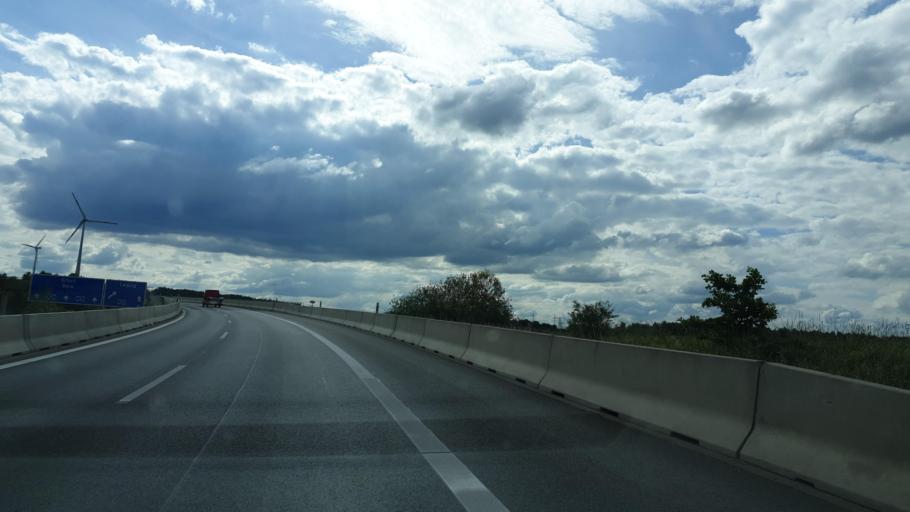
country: DE
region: Saxony
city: Wittgensdorf
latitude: 50.8532
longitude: 12.8499
